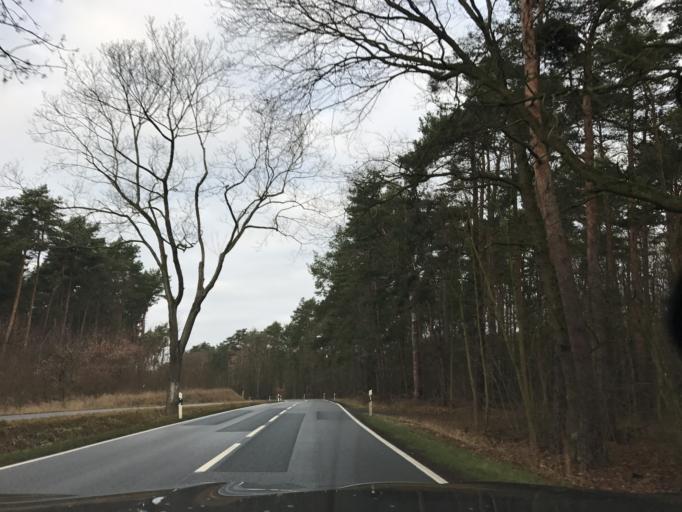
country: DE
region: Brandenburg
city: Golzow
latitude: 52.3446
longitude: 12.6394
